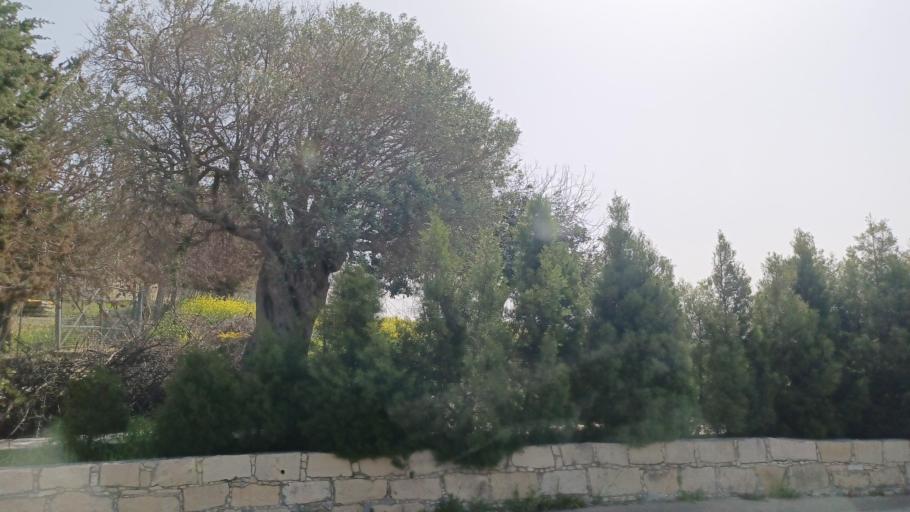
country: CY
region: Limassol
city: Pissouri
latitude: 34.7115
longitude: 32.7087
